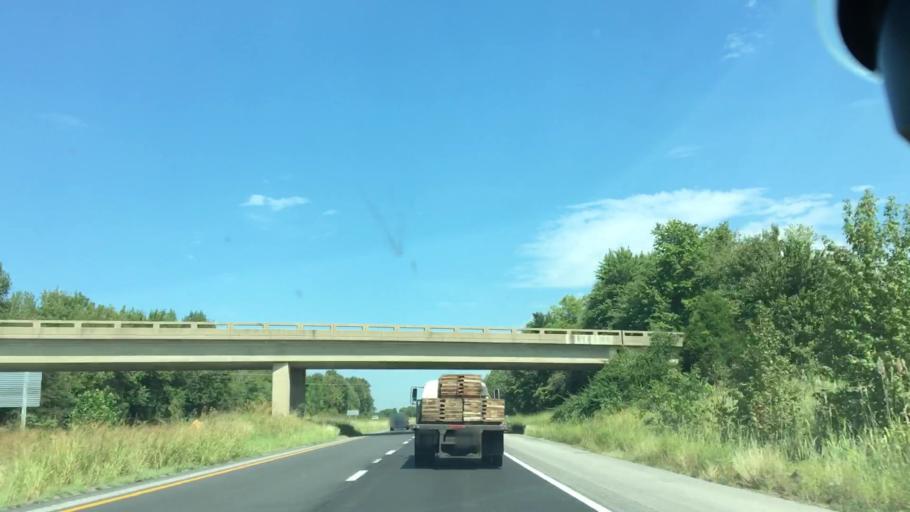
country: US
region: Kentucky
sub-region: Hopkins County
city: Madisonville
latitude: 37.3807
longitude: -87.4821
